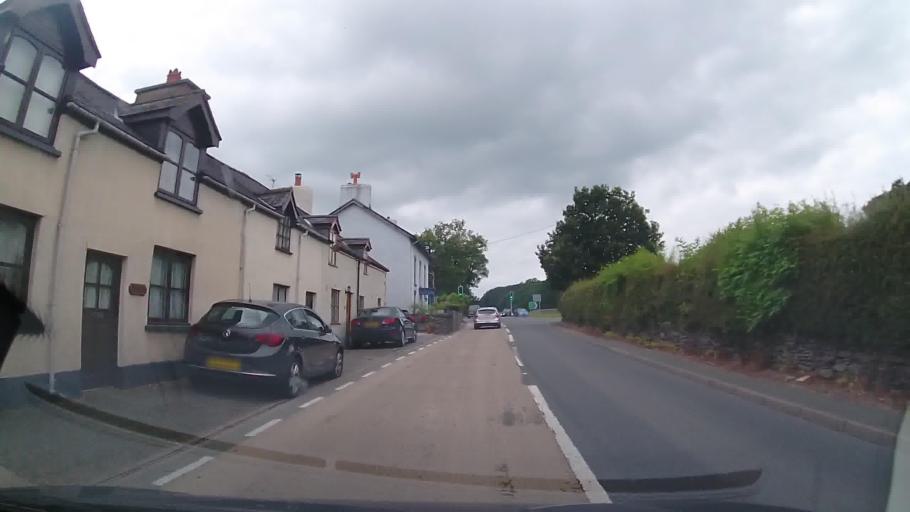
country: GB
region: Wales
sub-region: Denbighshire
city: Corwen
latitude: 52.9820
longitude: -3.3957
